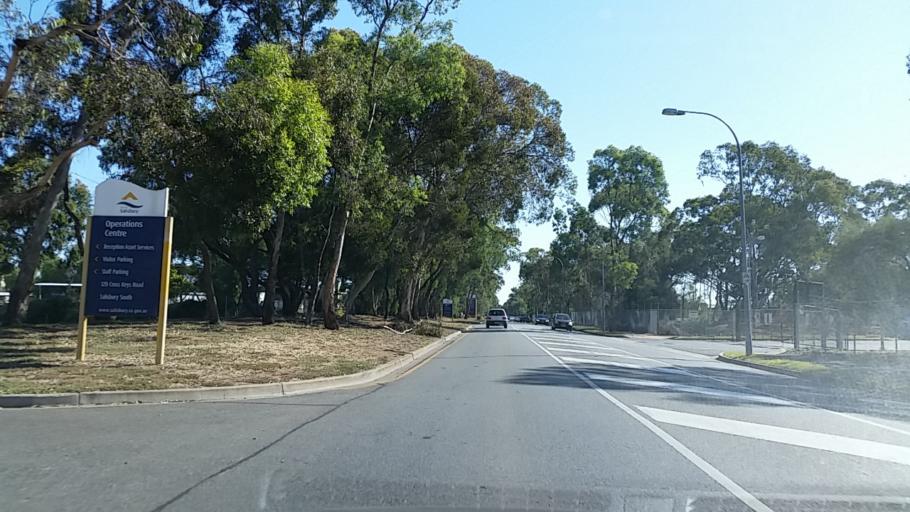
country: AU
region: South Australia
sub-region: Salisbury
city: Salisbury
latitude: -34.7795
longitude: 138.6419
